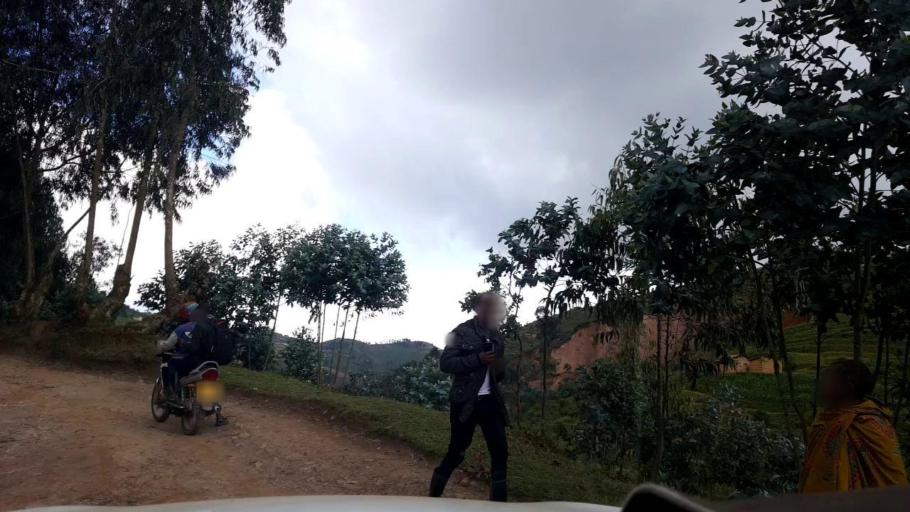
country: RW
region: Western Province
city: Kibuye
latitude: -1.8925
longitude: 29.4632
